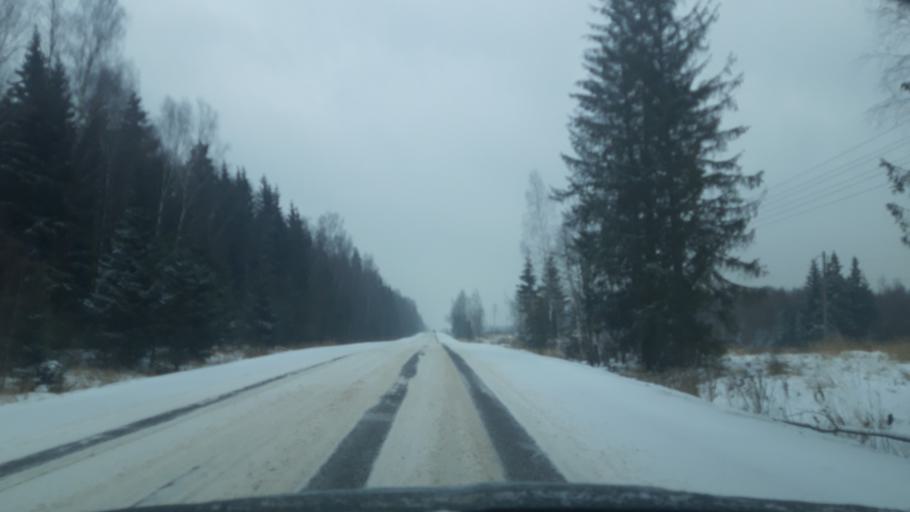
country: RU
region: Moskovskaya
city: Avtopoligon
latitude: 56.2629
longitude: 37.2881
